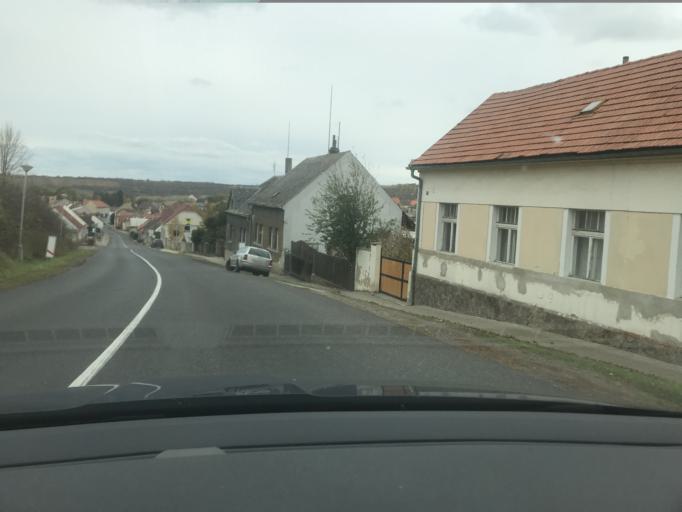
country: CZ
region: Ustecky
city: Trebenice
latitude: 50.4799
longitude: 13.9972
